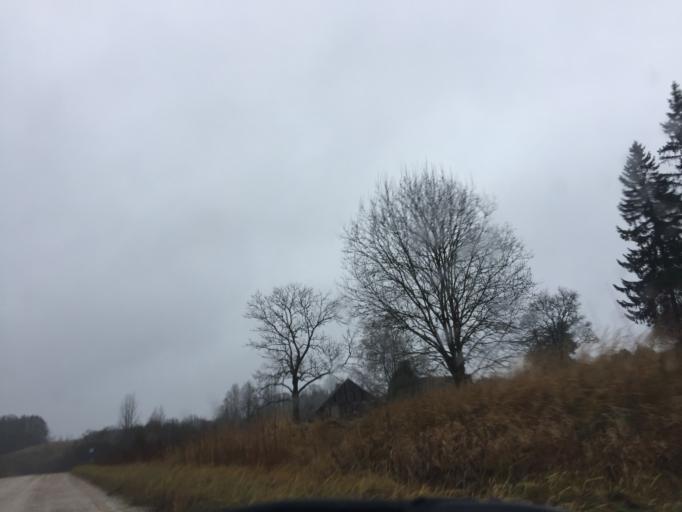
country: LV
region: Salas
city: Sala
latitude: 56.4911
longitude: 25.6735
